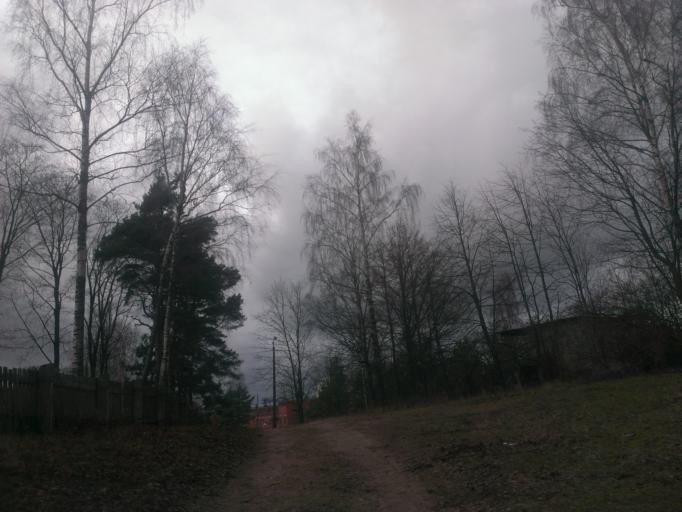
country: LV
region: Riga
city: Bolderaja
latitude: 57.0421
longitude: 24.0908
